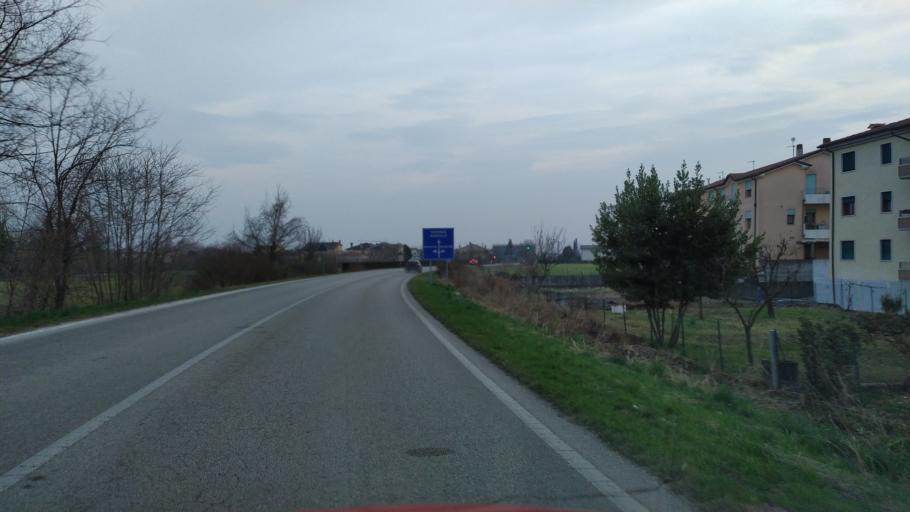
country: IT
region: Veneto
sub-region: Provincia di Vicenza
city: Dueville
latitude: 45.6440
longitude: 11.5572
